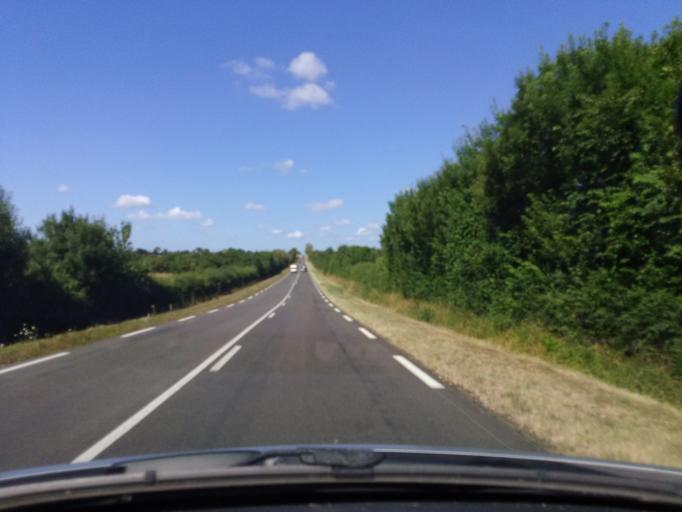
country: FR
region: Pays de la Loire
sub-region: Departement de la Vendee
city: Moutiers-les-Mauxfaits
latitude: 46.4573
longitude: -1.3704
